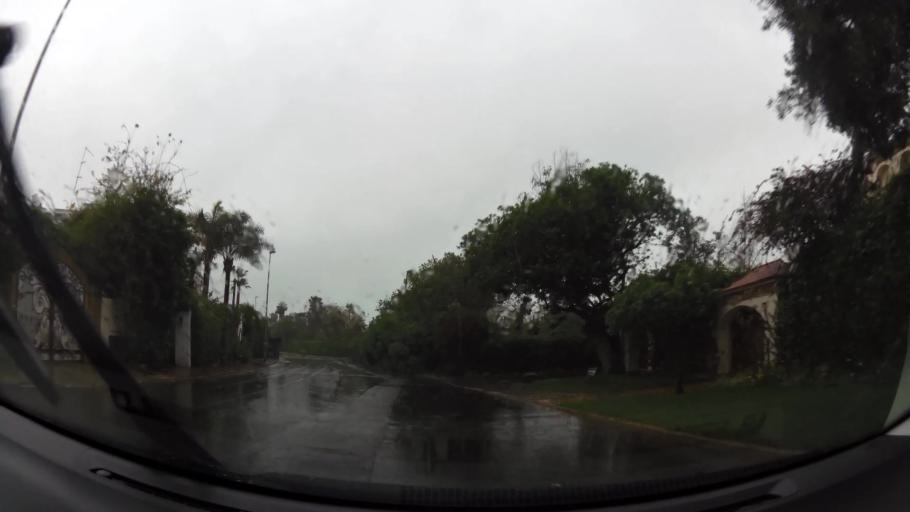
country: MA
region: Grand Casablanca
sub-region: Casablanca
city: Casablanca
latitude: 33.5893
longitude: -7.6723
